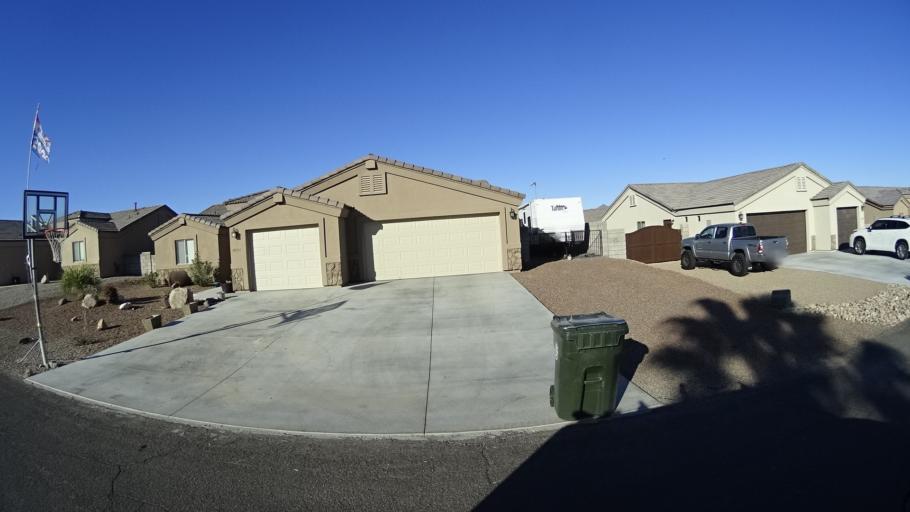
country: US
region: Arizona
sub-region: Mohave County
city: Kingman
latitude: 35.2133
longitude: -114.0043
